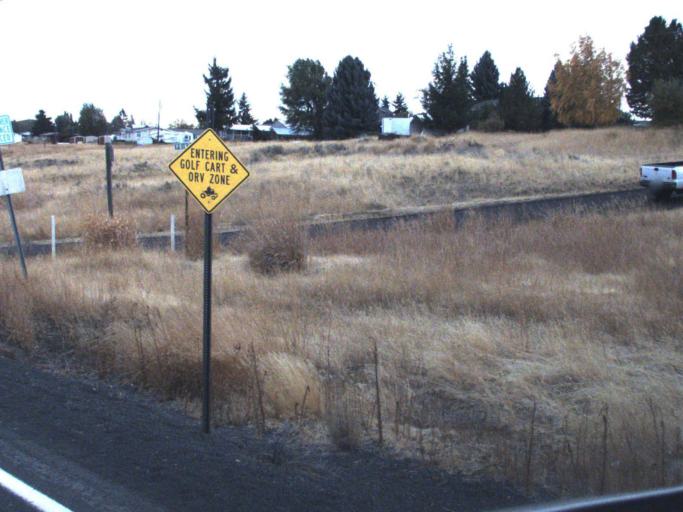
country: US
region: Washington
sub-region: Okanogan County
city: Coulee Dam
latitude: 47.7582
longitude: -118.7164
